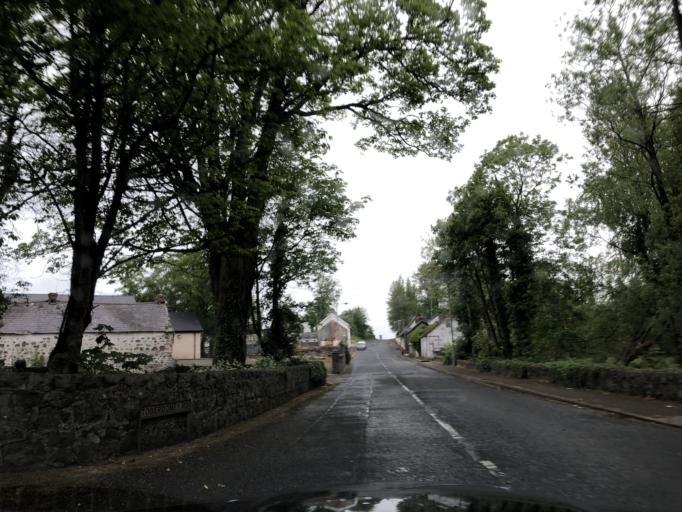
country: GB
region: Northern Ireland
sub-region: Ballymoney District
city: Ballymoney
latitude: 55.1239
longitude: -6.4689
